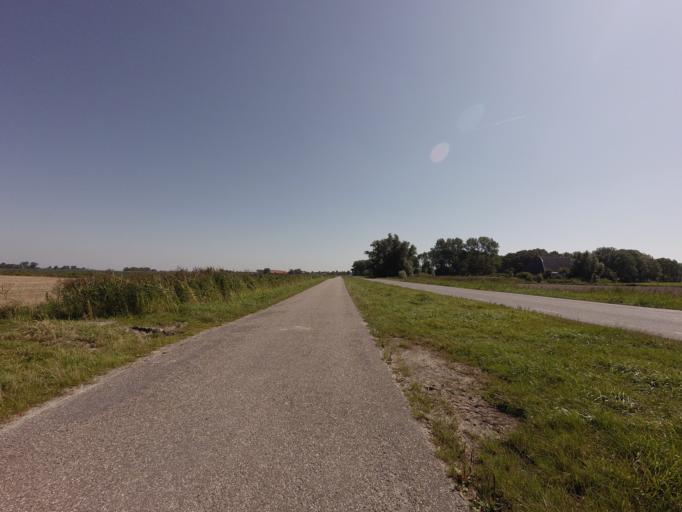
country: NL
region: Friesland
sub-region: Gemeente Dongeradeel
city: Ternaard
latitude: 53.3817
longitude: 6.0339
